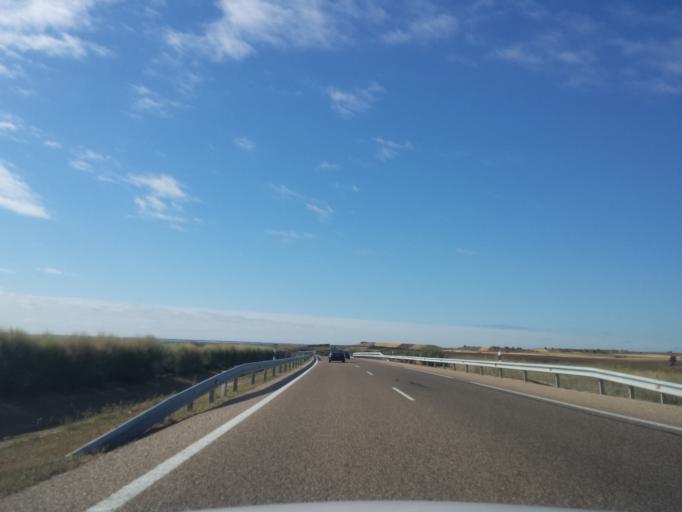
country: ES
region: Castille and Leon
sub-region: Provincia de Leon
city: Algadefe
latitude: 42.2169
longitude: -5.6002
